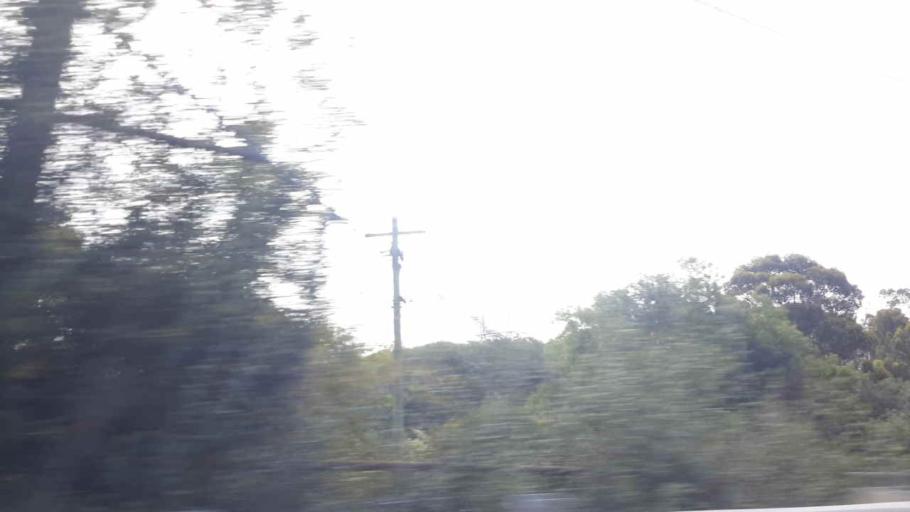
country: AU
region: New South Wales
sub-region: Campbelltown Municipality
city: Glen Alpine
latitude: -34.0903
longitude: 150.7727
